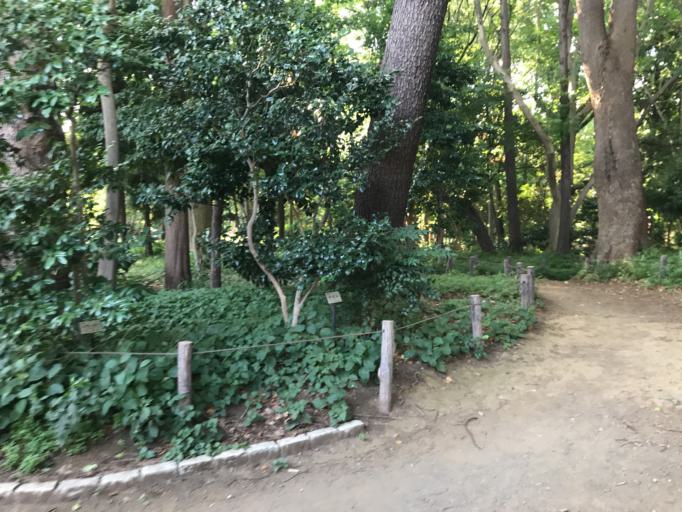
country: JP
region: Tokyo
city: Tokyo
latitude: 35.6256
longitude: 139.7069
